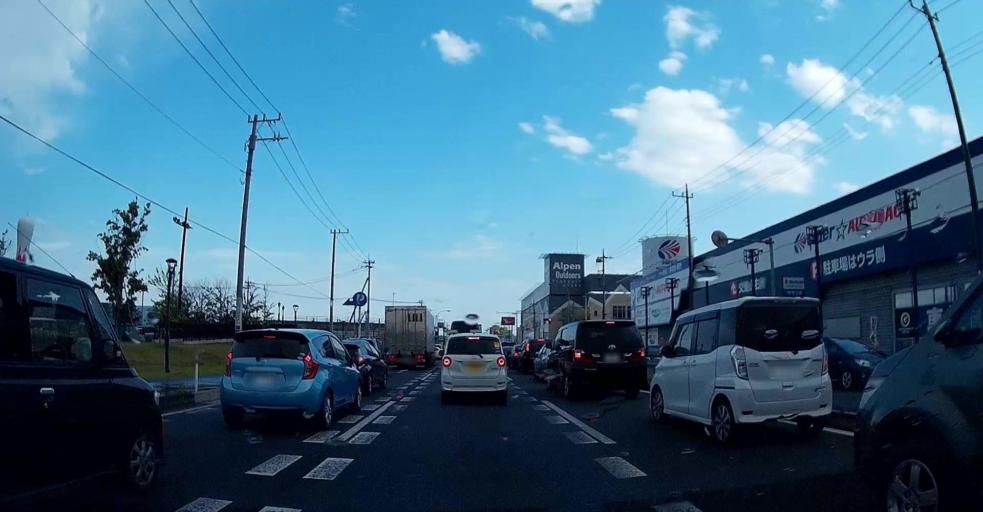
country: JP
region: Chiba
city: Abiko
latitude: 35.8310
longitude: 140.0128
